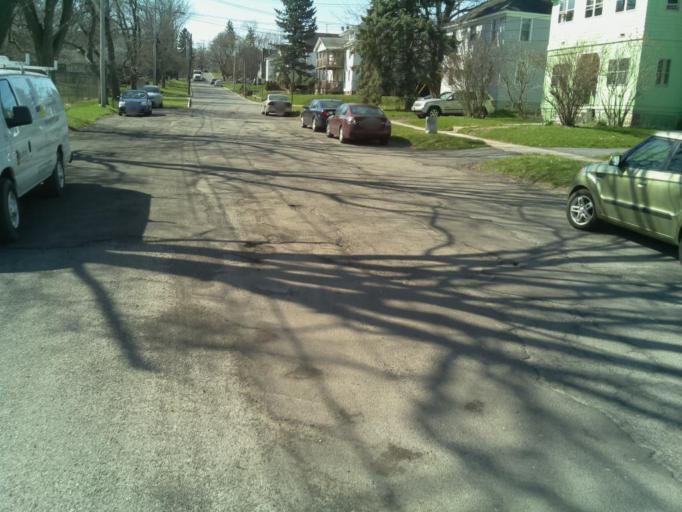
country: US
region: New York
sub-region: Onondaga County
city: East Syracuse
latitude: 43.0714
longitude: -76.1000
